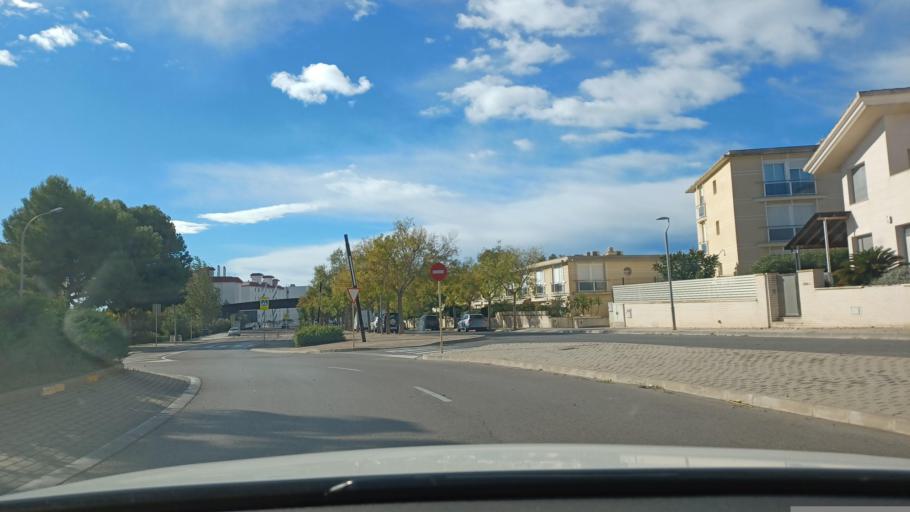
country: ES
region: Catalonia
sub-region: Provincia de Tarragona
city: Sant Carles de la Rapita
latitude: 40.6081
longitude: 0.5833
